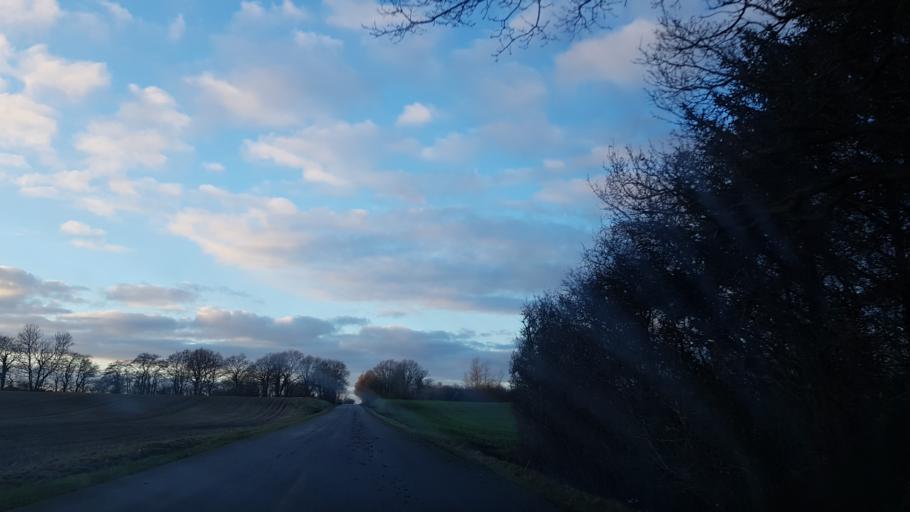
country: DK
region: South Denmark
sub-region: Kolding Kommune
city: Vamdrup
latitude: 55.3661
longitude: 9.3200
